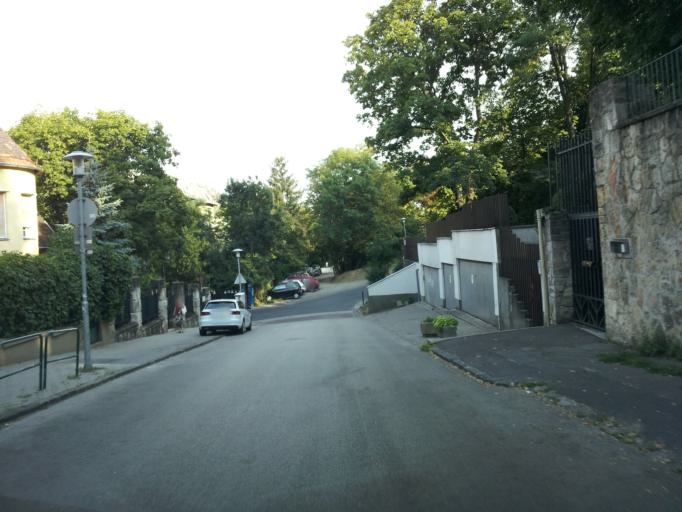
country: HU
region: Budapest
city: Budapest XII. keruelet
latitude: 47.5037
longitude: 19.0176
